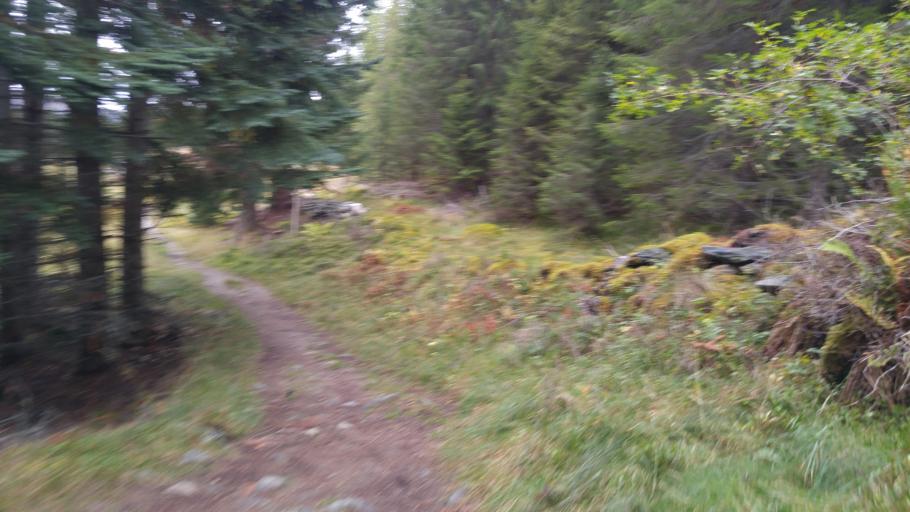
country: NO
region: Sor-Trondelag
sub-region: Trondheim
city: Trondheim
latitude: 63.4227
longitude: 10.3126
